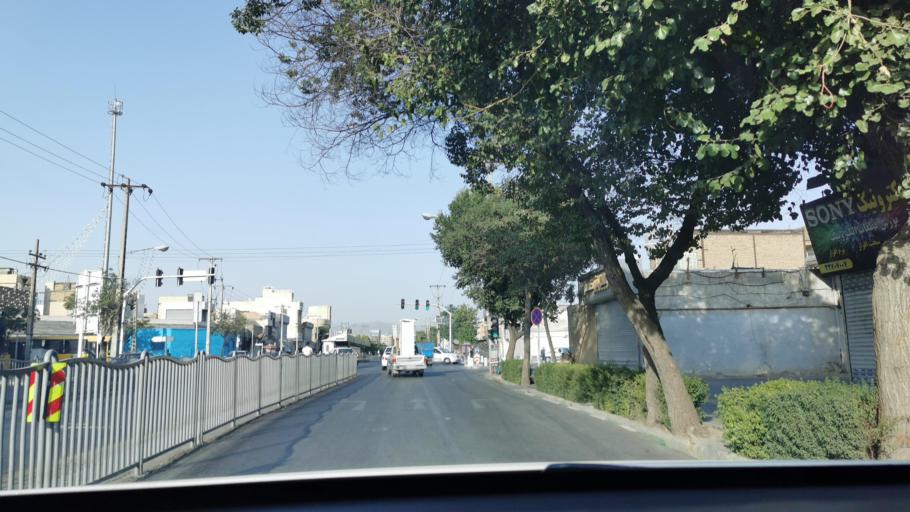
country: IR
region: Razavi Khorasan
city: Mashhad
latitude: 36.3022
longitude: 59.6384
